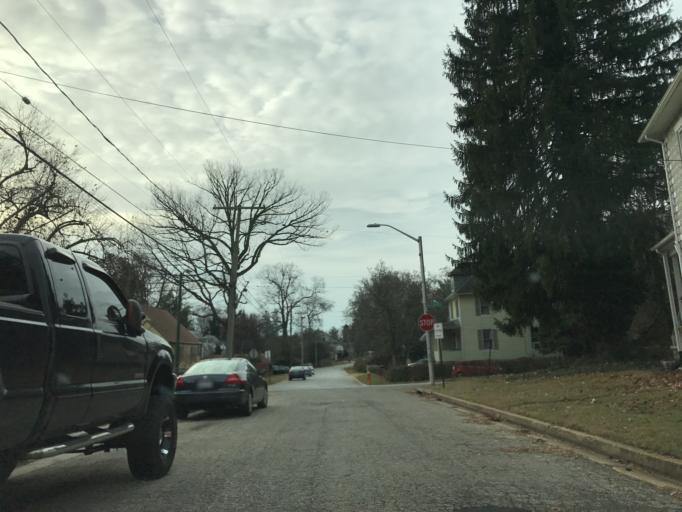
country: US
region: Maryland
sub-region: Baltimore County
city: Overlea
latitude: 39.3546
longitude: -76.5371
